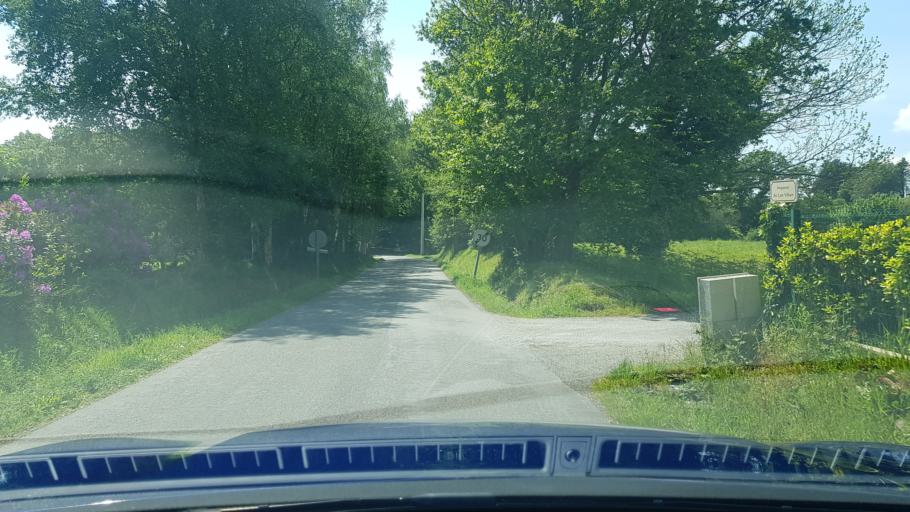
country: FR
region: Brittany
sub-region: Departement du Morbihan
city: Gestel
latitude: 47.8081
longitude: -3.4329
